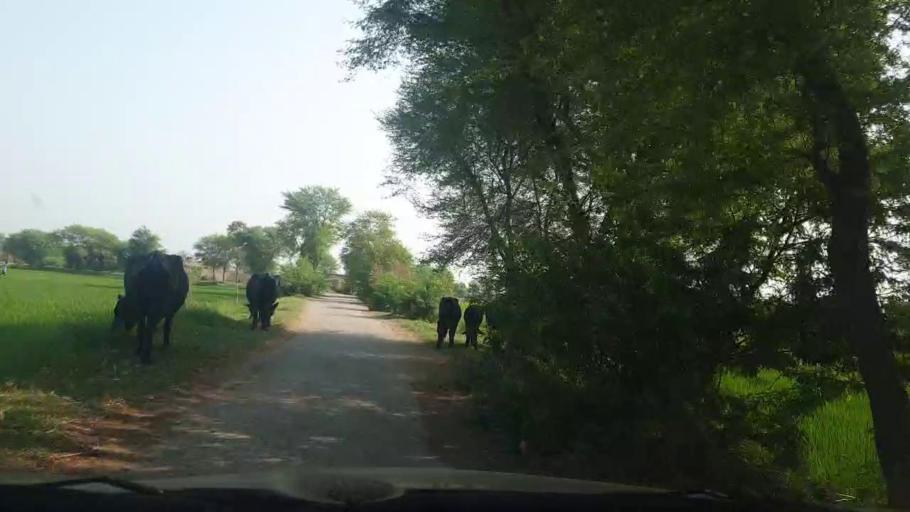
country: PK
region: Sindh
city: Larkana
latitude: 27.5936
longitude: 68.1606
